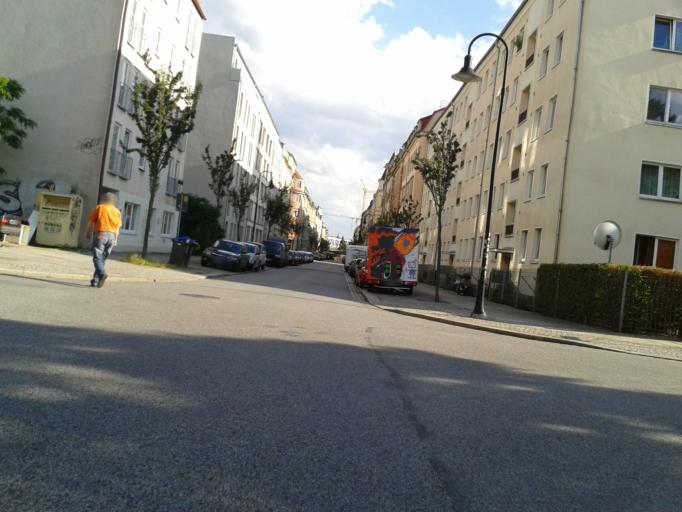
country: DE
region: Saxony
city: Albertstadt
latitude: 51.0762
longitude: 13.7471
